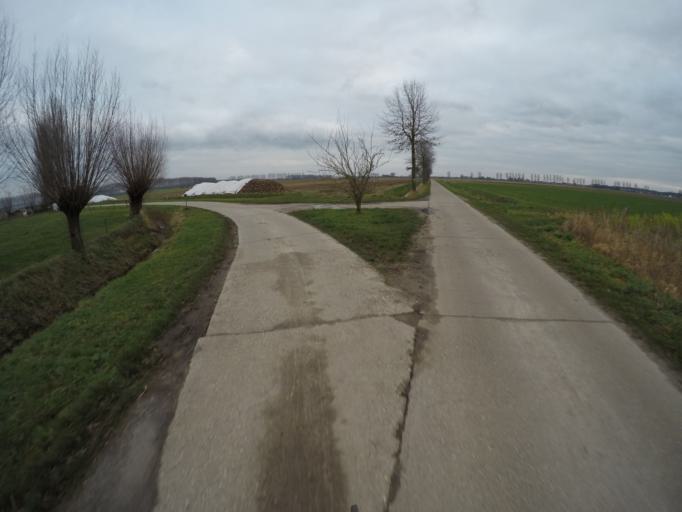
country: BE
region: Flanders
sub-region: Provincie Oost-Vlaanderen
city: Sint-Gillis-Waas
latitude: 51.2531
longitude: 4.1034
